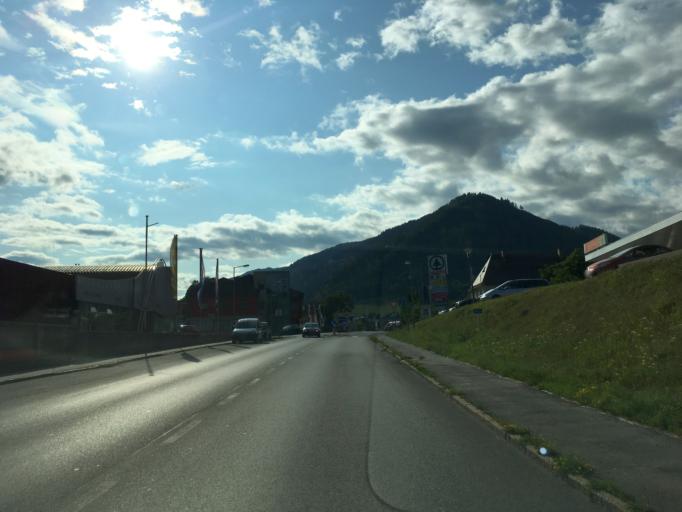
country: AT
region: Styria
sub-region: Politischer Bezirk Murau
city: Murau
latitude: 47.1124
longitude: 14.1803
